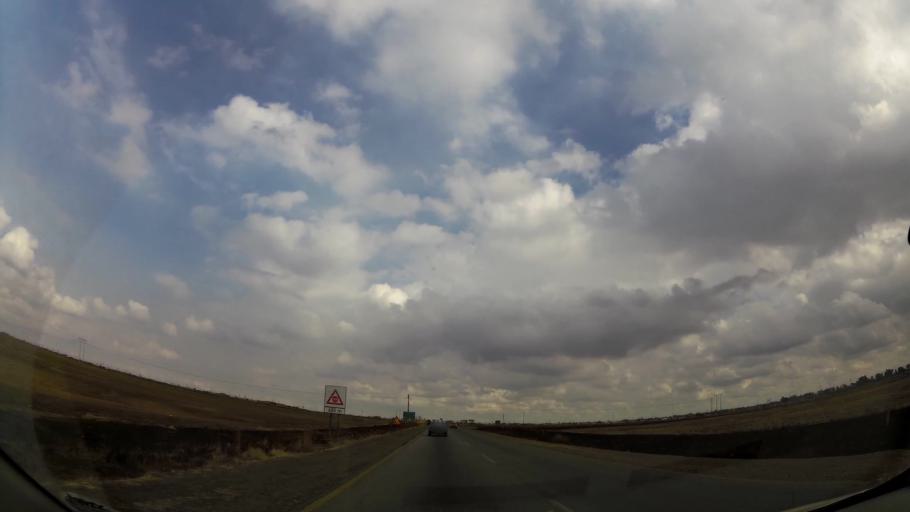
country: ZA
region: Orange Free State
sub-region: Fezile Dabi District Municipality
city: Sasolburg
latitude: -26.8441
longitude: 27.8910
